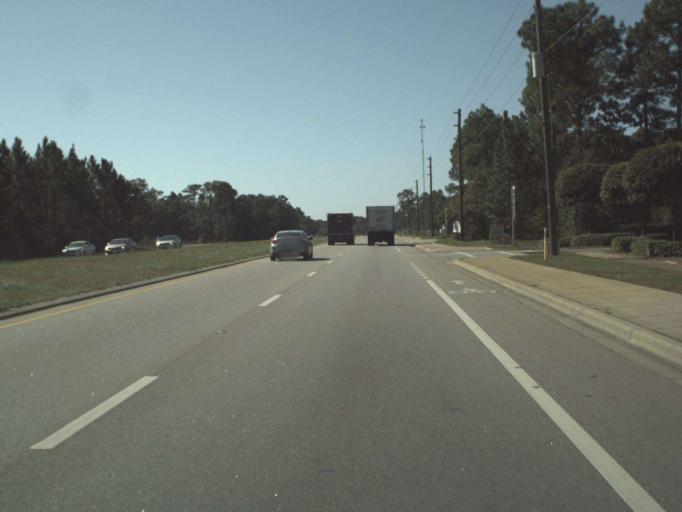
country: US
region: Florida
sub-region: Walton County
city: Seaside
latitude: 30.3830
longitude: -86.1768
